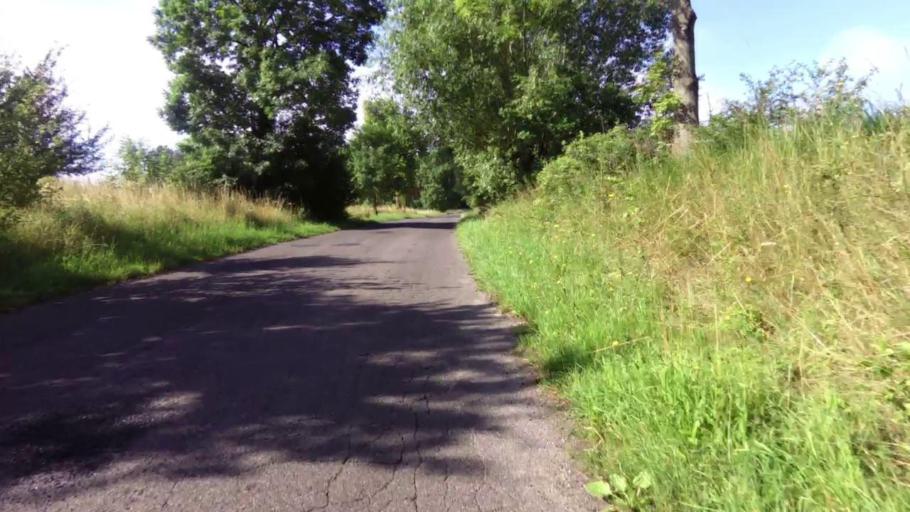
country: PL
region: West Pomeranian Voivodeship
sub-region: Powiat stargardzki
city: Marianowo
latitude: 53.3771
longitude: 15.2632
